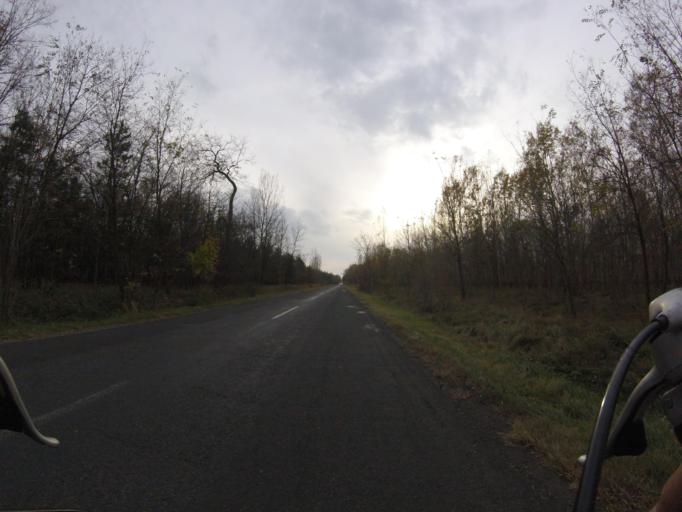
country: HU
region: Pest
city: Csemo
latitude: 47.0999
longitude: 19.6169
